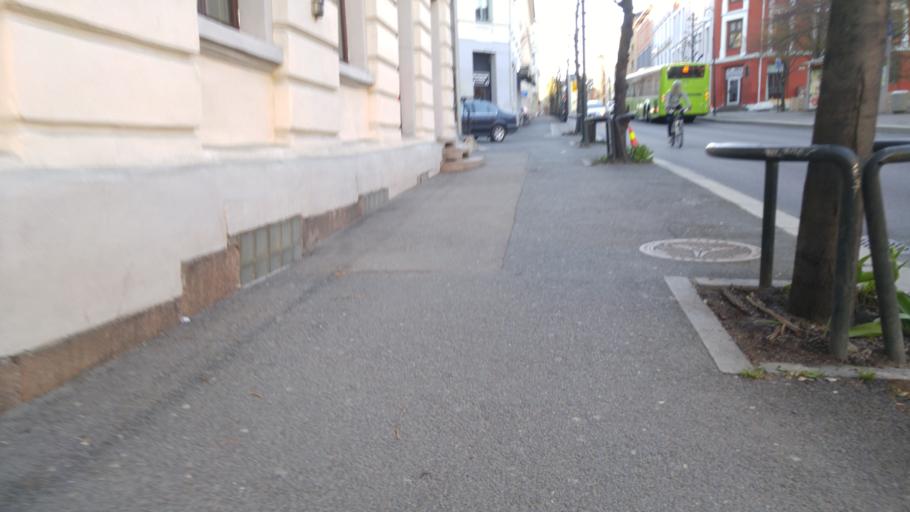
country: NO
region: Oslo
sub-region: Oslo
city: Oslo
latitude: 59.9086
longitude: 10.7688
